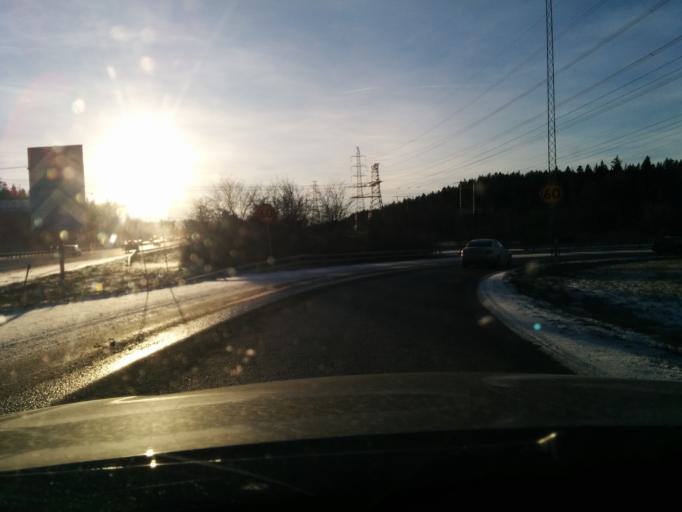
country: SE
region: Stockholm
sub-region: Sollentuna Kommun
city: Sollentuna
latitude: 59.4354
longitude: 17.9238
